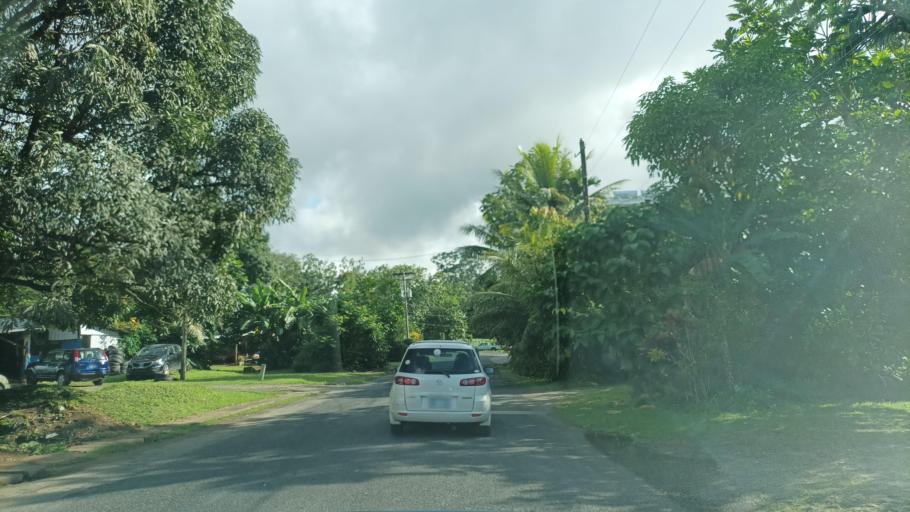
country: FM
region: Pohnpei
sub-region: Kolonia Municipality
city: Kolonia
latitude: 6.9595
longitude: 158.2086
